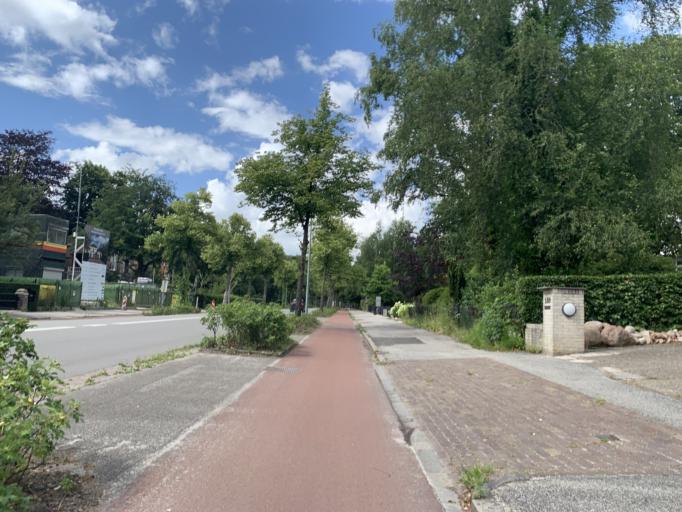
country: NL
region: Groningen
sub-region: Gemeente Haren
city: Haren
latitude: 53.1908
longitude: 6.5843
